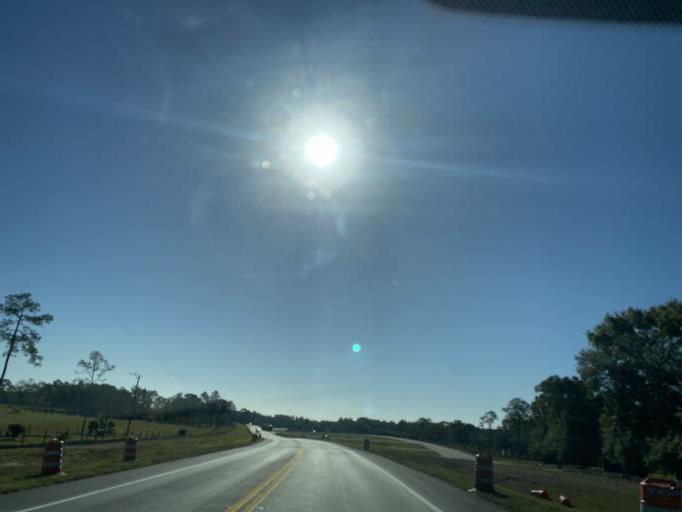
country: US
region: Florida
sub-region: Lake County
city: Mount Plymouth
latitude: 28.8362
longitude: -81.5262
